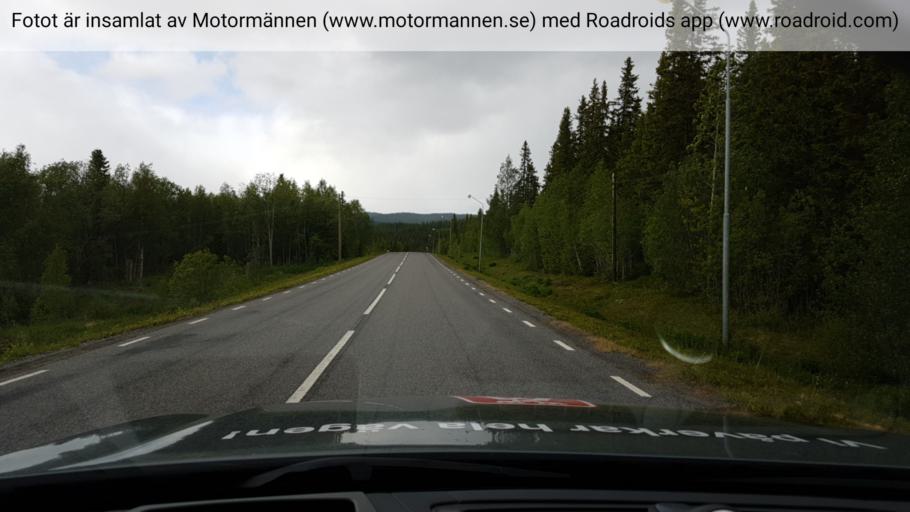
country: SE
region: Jaemtland
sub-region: Are Kommun
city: Are
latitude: 63.6485
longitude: 13.0689
